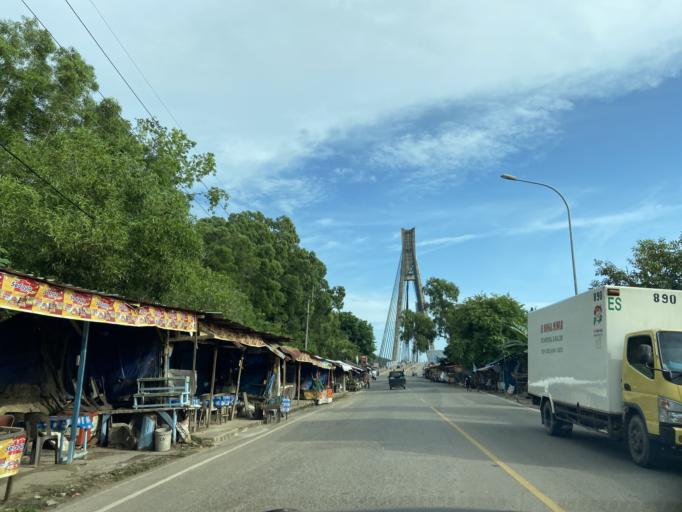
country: SG
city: Singapore
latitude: 0.9776
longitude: 104.0443
